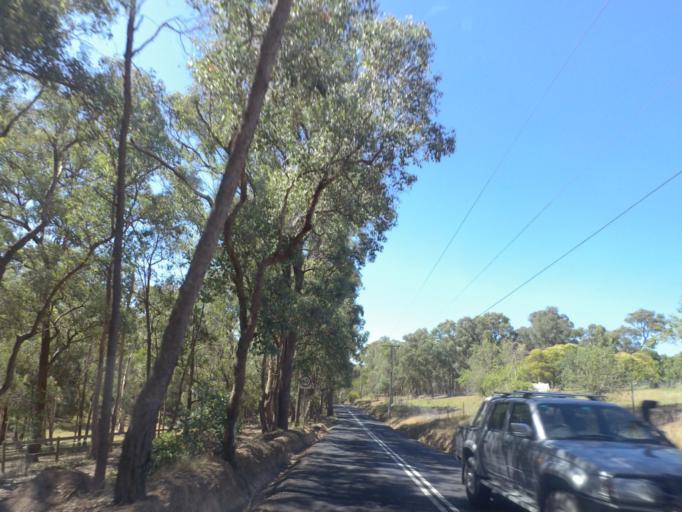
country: AU
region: Victoria
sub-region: Maroondah
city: Warranwood
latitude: -37.7576
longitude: 145.2541
